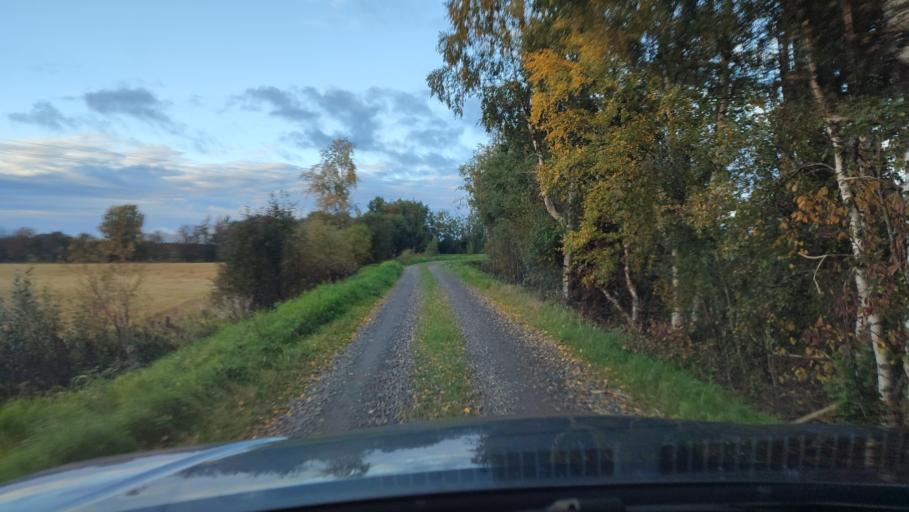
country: FI
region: Ostrobothnia
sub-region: Sydosterbotten
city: Kristinestad
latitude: 62.2336
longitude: 21.4509
